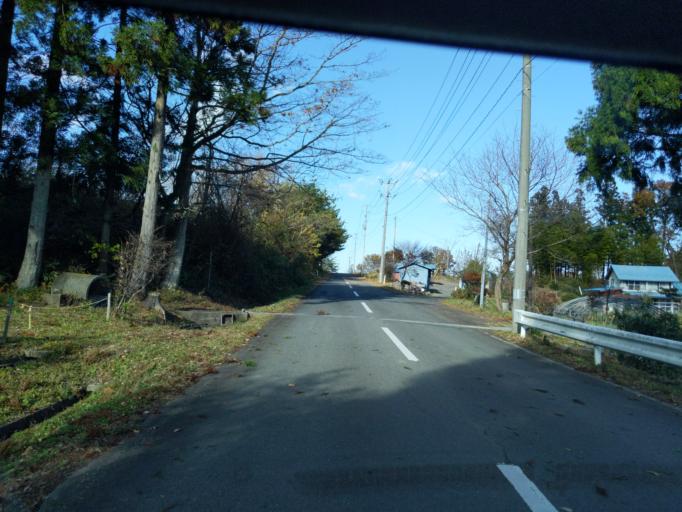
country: JP
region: Iwate
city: Mizusawa
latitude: 39.0616
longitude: 141.1128
